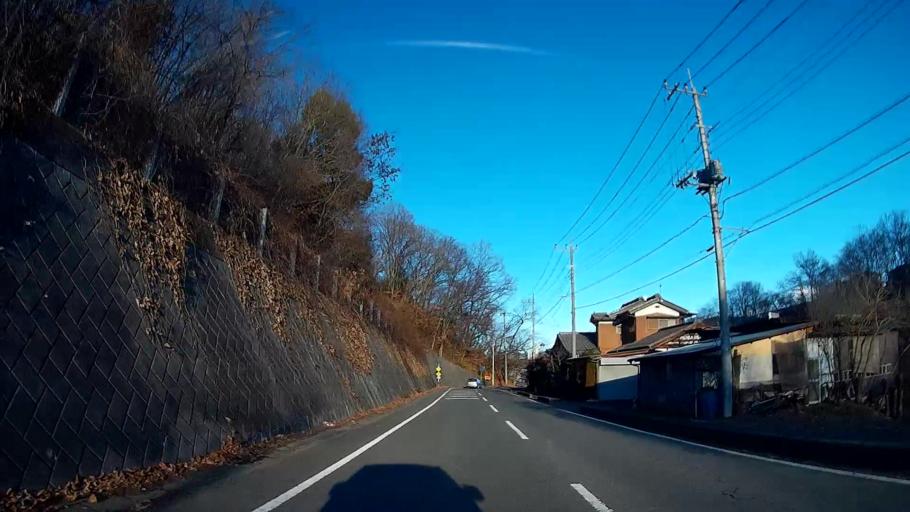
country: JP
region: Saitama
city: Chichibu
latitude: 36.0414
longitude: 139.0313
